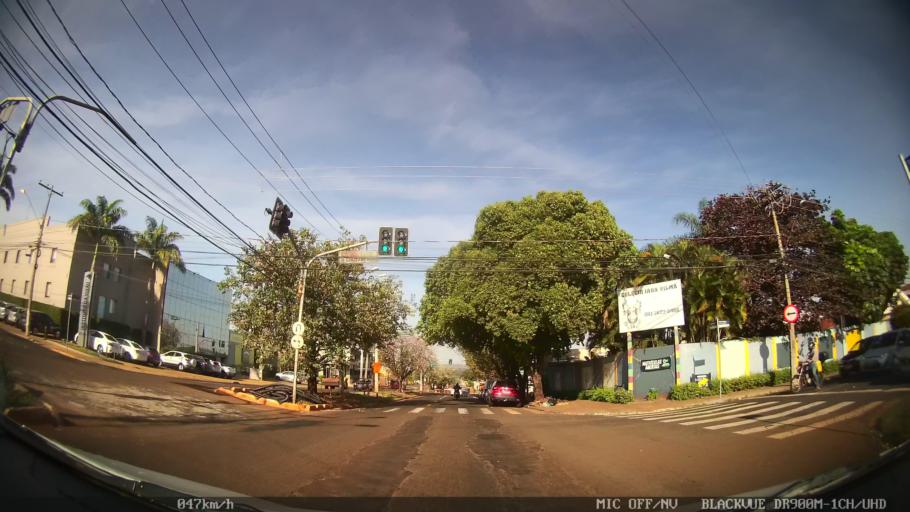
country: BR
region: Sao Paulo
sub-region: Ribeirao Preto
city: Ribeirao Preto
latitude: -21.1970
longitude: -47.8145
